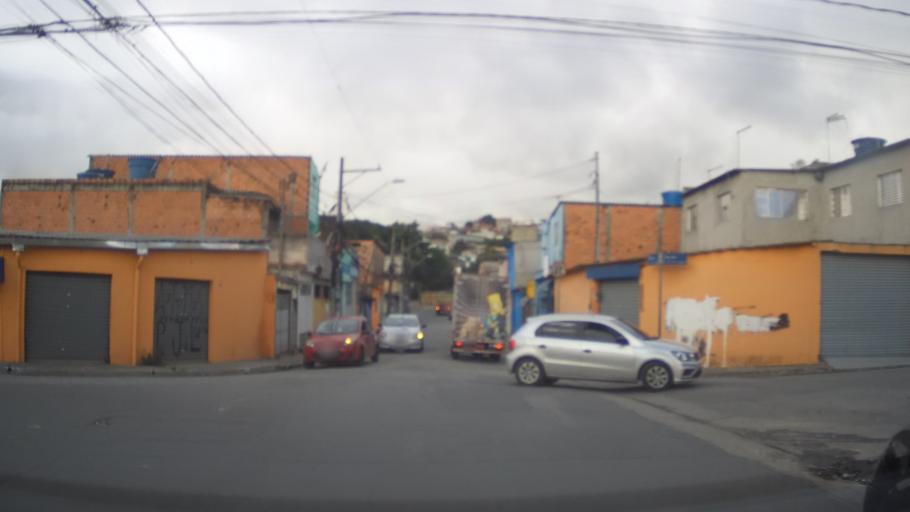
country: BR
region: Sao Paulo
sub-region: Itaquaquecetuba
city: Itaquaquecetuba
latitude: -23.4467
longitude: -46.4204
